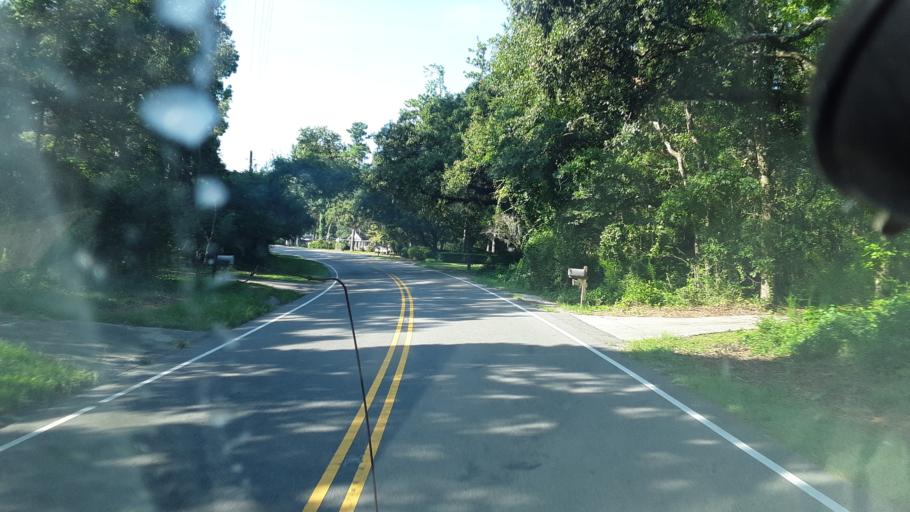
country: US
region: North Carolina
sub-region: Brunswick County
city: Belville
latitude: 34.2146
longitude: -77.9834
